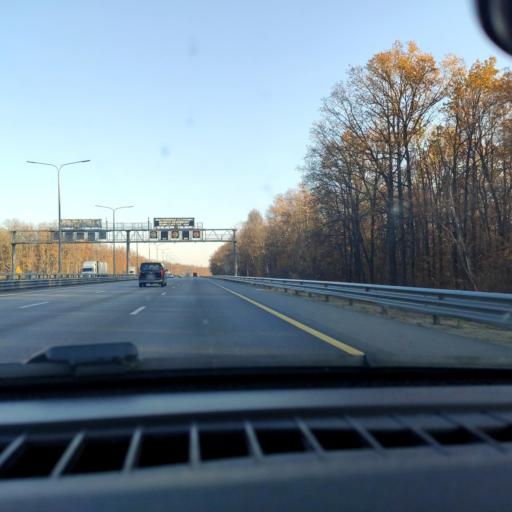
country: RU
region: Voronezj
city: Podgornoye
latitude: 51.8342
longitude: 39.2318
